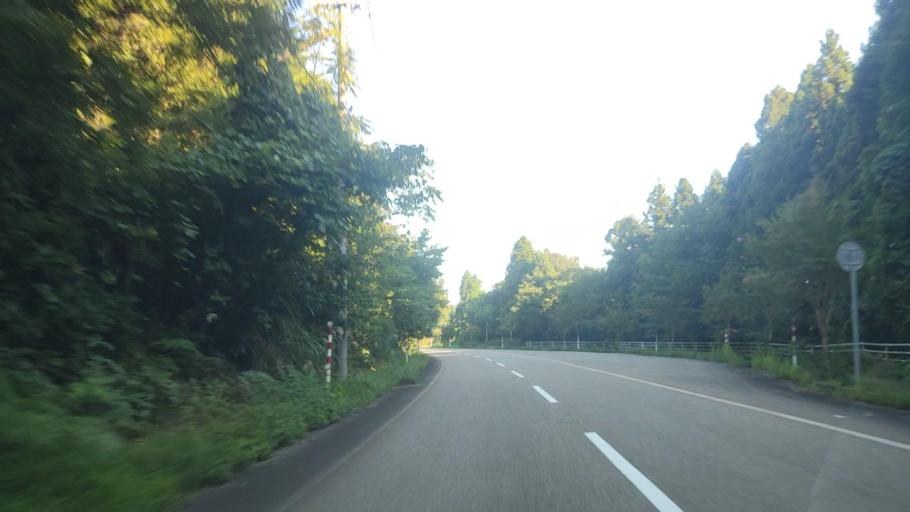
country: JP
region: Ishikawa
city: Nanao
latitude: 37.1258
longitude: 136.9258
